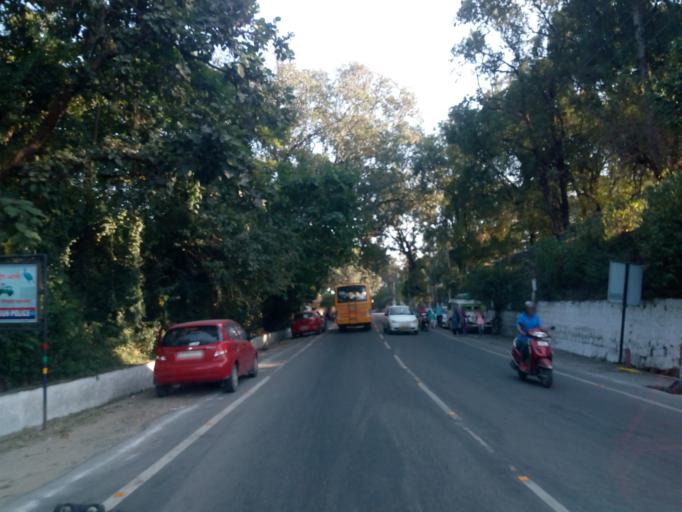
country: IN
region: Uttarakhand
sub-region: Dehradun
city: Dehradun
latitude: 30.3455
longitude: 78.0473
